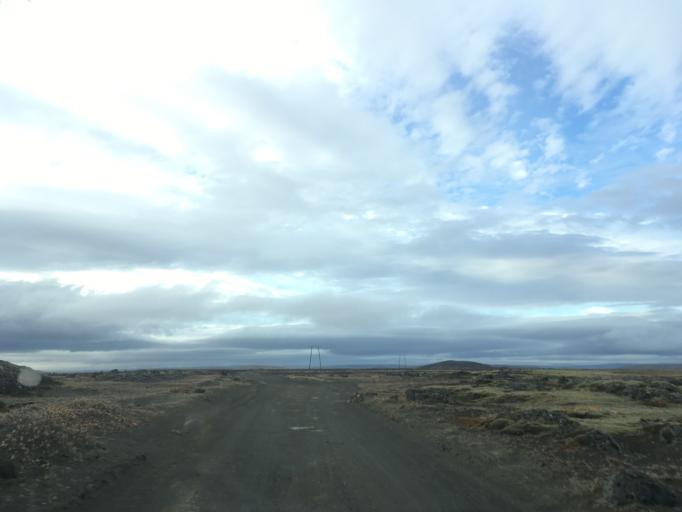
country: IS
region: South
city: Vestmannaeyjar
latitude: 64.1051
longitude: -19.1037
